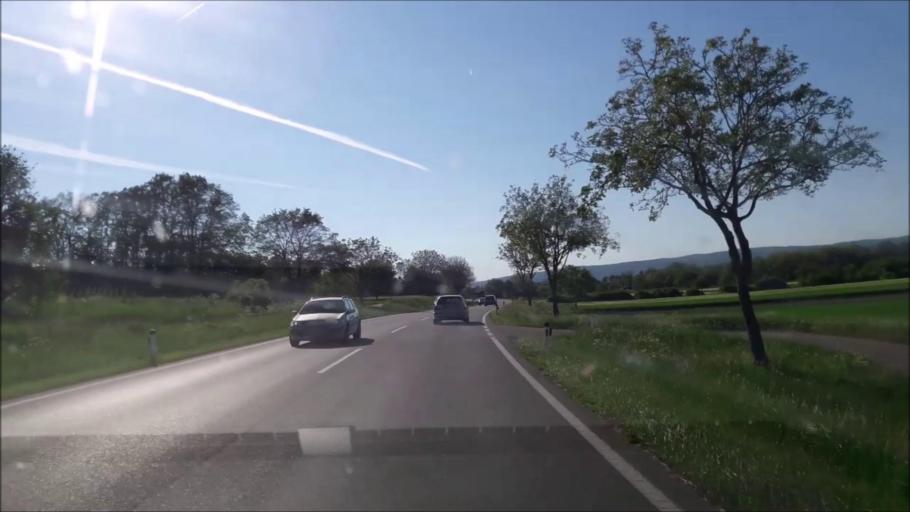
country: AT
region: Burgenland
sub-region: Eisenstadt-Umgebung
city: Trausdorf an der Wulka
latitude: 47.8124
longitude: 16.5753
